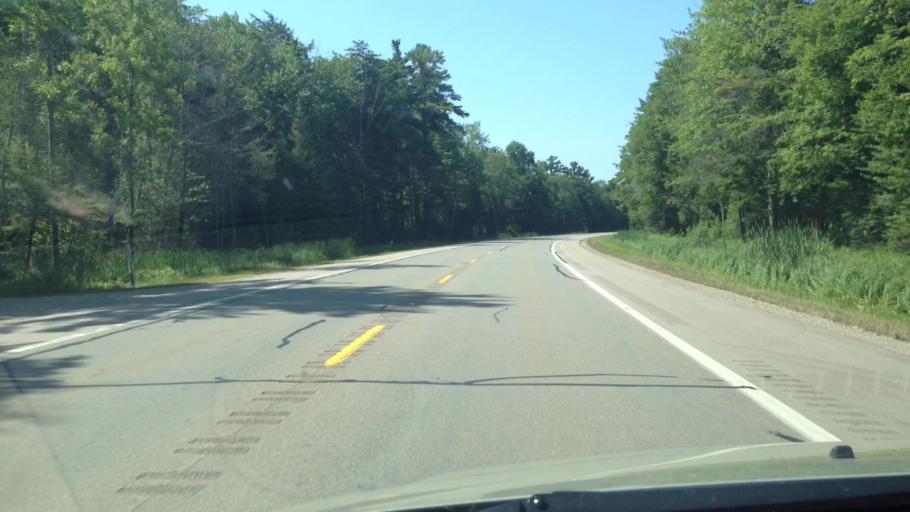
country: US
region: Michigan
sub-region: Menominee County
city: Menominee
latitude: 45.2960
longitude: -87.4404
